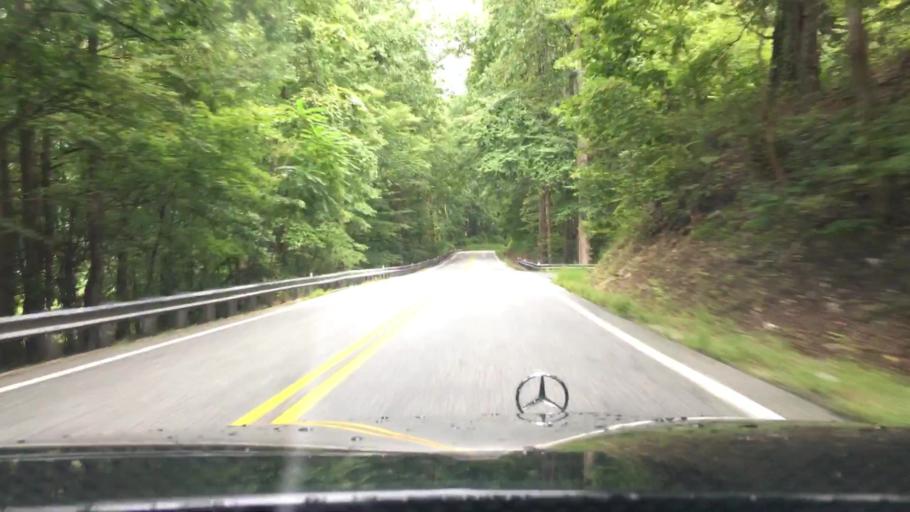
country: US
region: Virginia
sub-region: Nelson County
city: Nellysford
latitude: 37.8503
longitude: -78.9277
